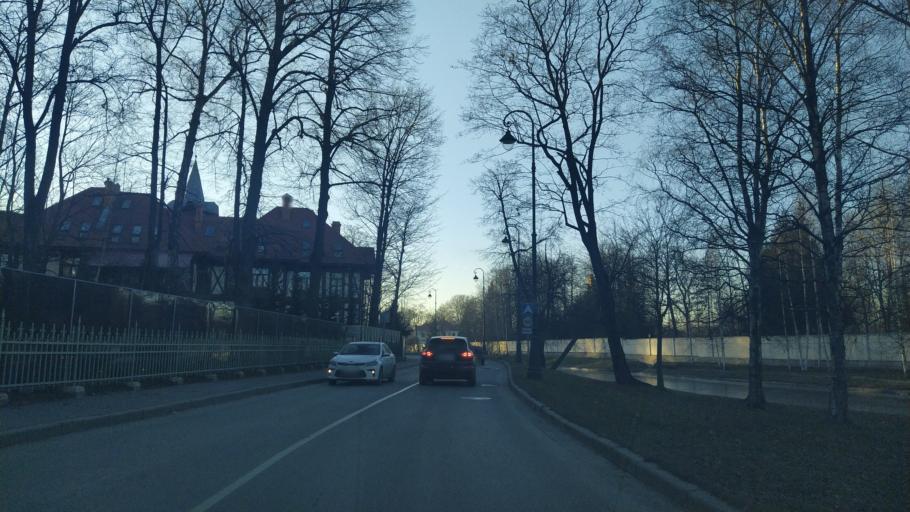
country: RU
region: St.-Petersburg
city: Novaya Derevnya
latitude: 59.9781
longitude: 30.2833
